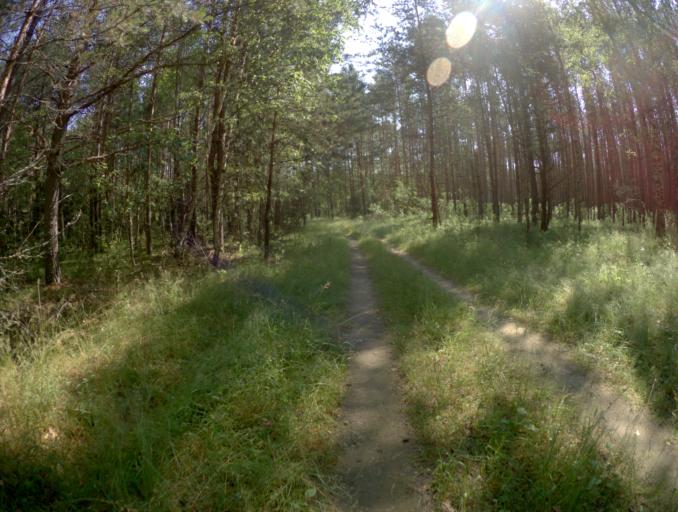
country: RU
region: Vladimir
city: Vyazniki
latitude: 56.3517
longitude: 42.1988
